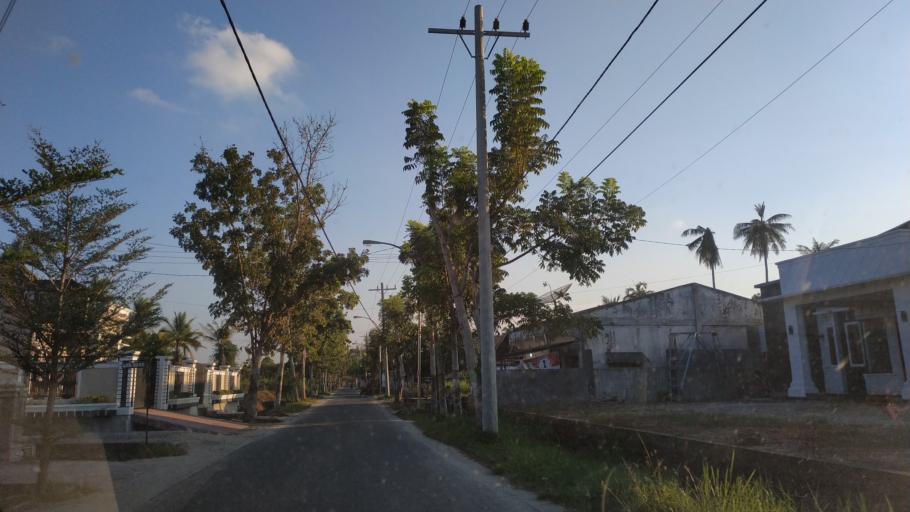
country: ID
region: North Sumatra
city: Tanjungbalai
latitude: 2.9457
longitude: 99.7879
